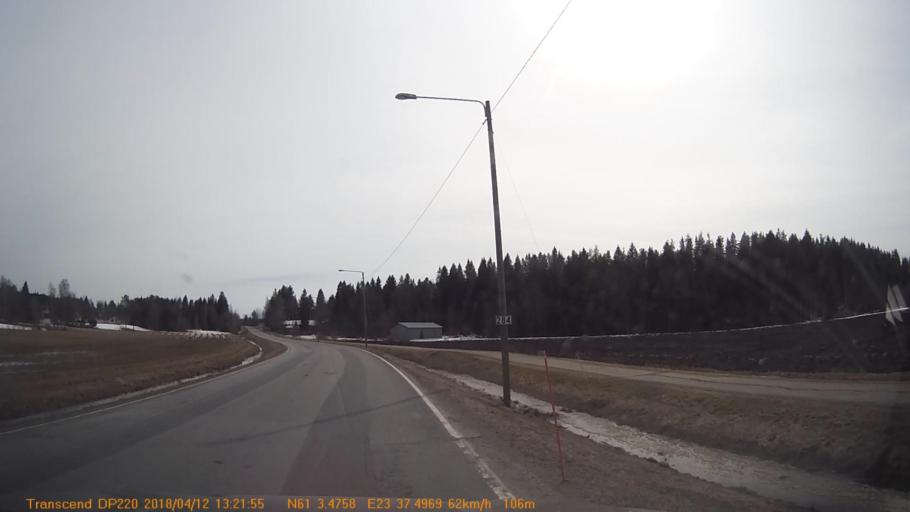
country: FI
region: Pirkanmaa
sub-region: Etelae-Pirkanmaa
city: Urjala
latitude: 61.0567
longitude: 23.6254
